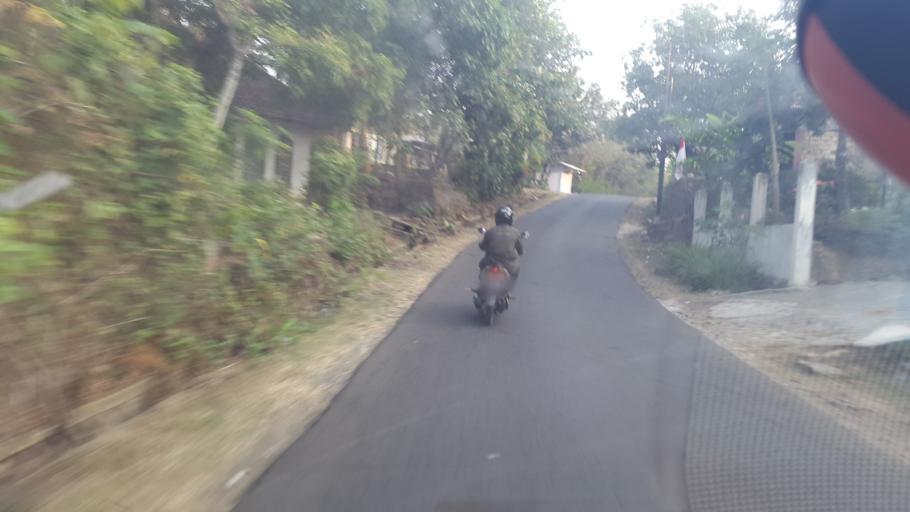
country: ID
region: West Java
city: Pondokaso
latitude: -7.3491
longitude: 106.5328
